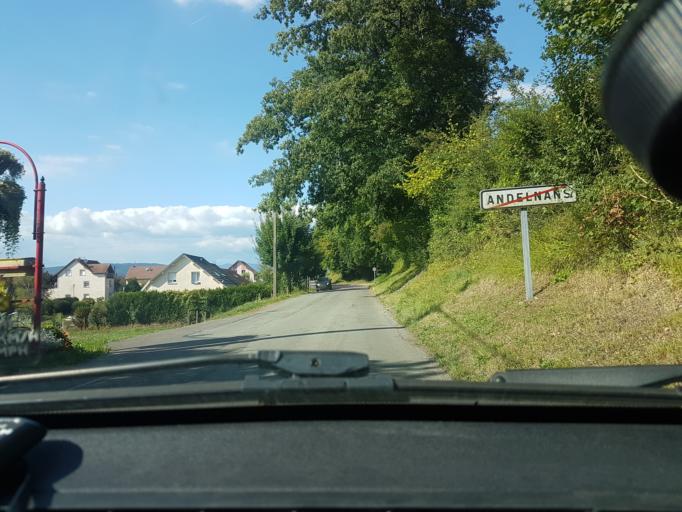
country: FR
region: Franche-Comte
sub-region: Territoire de Belfort
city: Danjoutin
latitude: 47.6100
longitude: 6.8673
